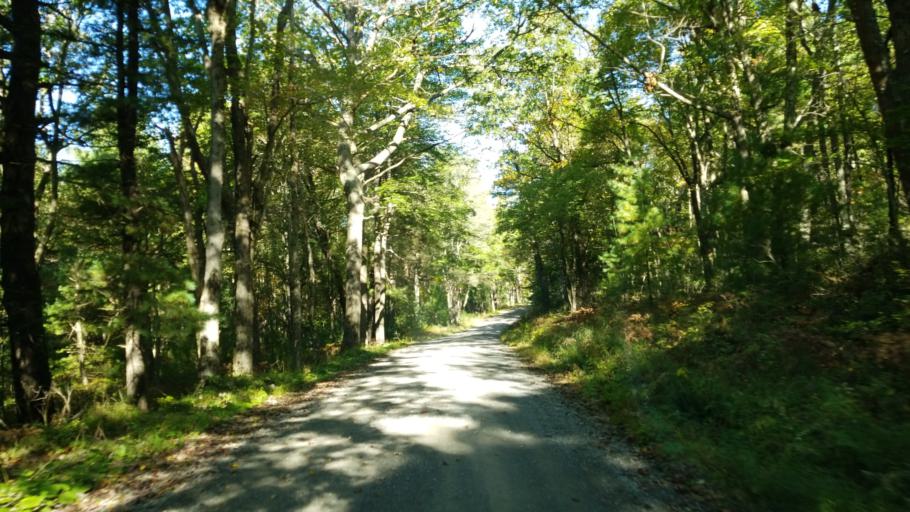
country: US
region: Pennsylvania
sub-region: Clearfield County
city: Hyde
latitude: 41.0826
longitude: -78.5250
